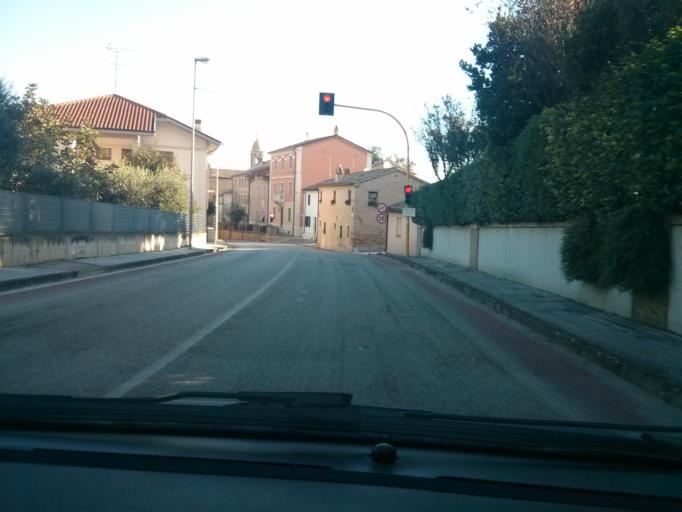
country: IT
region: The Marches
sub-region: Provincia di Pesaro e Urbino
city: Piagge
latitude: 43.7313
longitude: 12.9675
